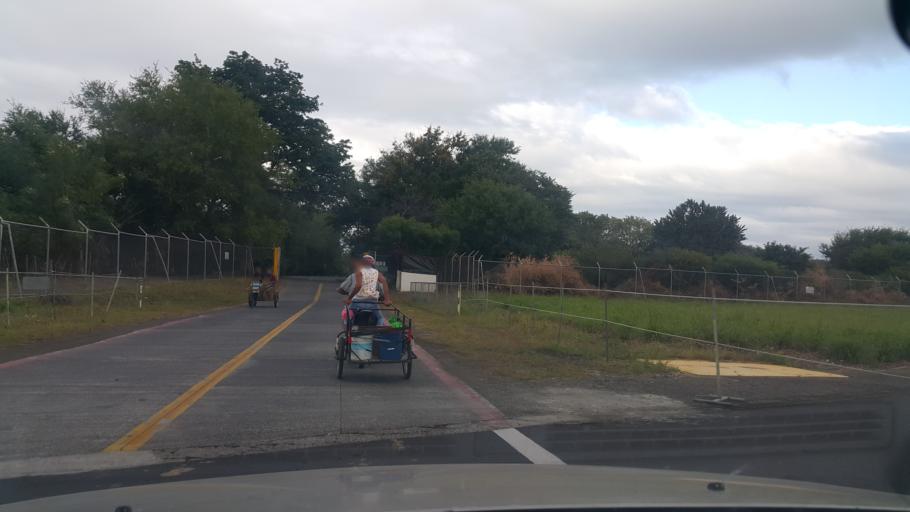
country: NI
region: Rivas
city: Moyogalpa
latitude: 11.5238
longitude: -85.7030
